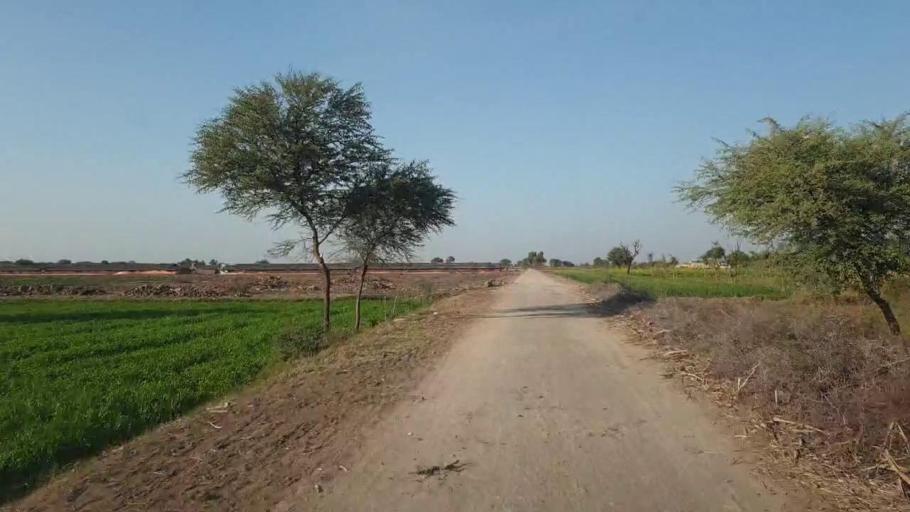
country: PK
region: Sindh
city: Tando Allahyar
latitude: 25.3738
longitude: 68.6979
